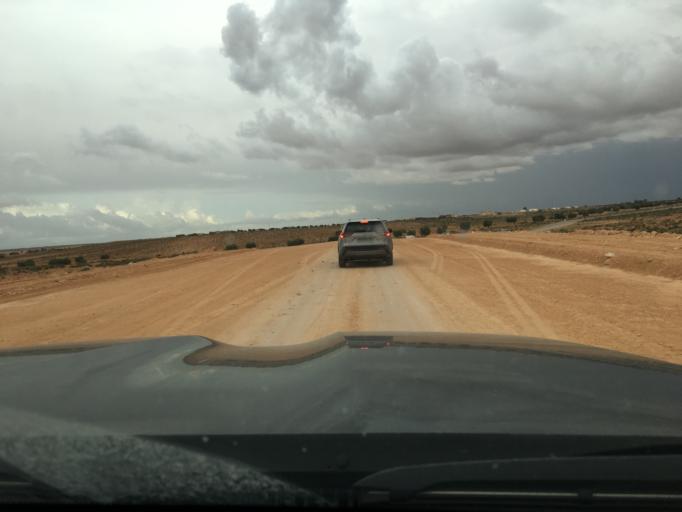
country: TN
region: Madanin
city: Medenine
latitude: 33.2861
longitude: 10.5997
